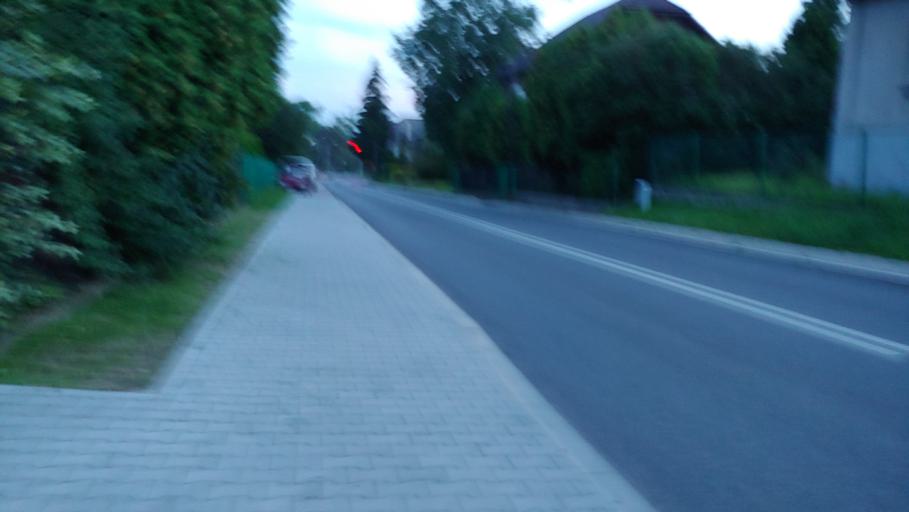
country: PL
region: Lesser Poland Voivodeship
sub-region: Powiat chrzanowski
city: Trzebinia
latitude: 50.1666
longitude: 19.4585
